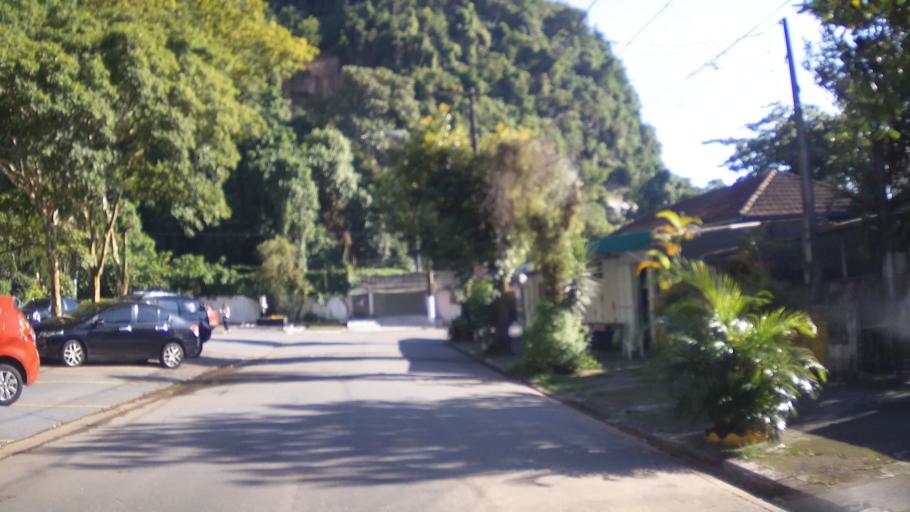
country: BR
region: Sao Paulo
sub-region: Santos
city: Santos
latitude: -23.9473
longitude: -46.3431
